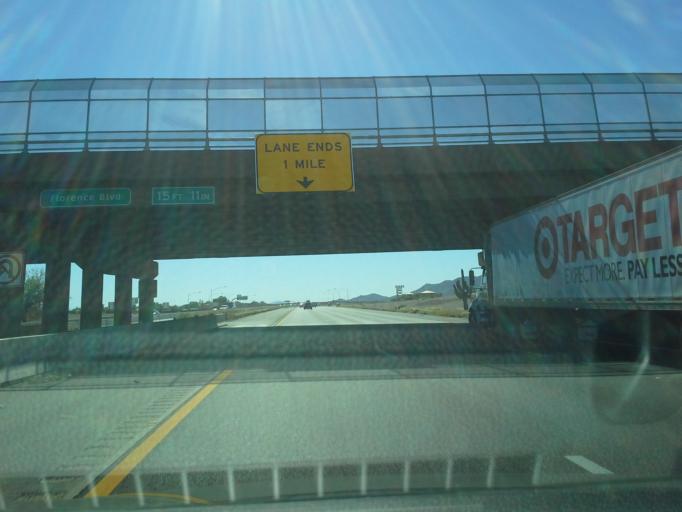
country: US
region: Arizona
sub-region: Pinal County
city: Casa Grande
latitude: 32.8802
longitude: -111.6870
